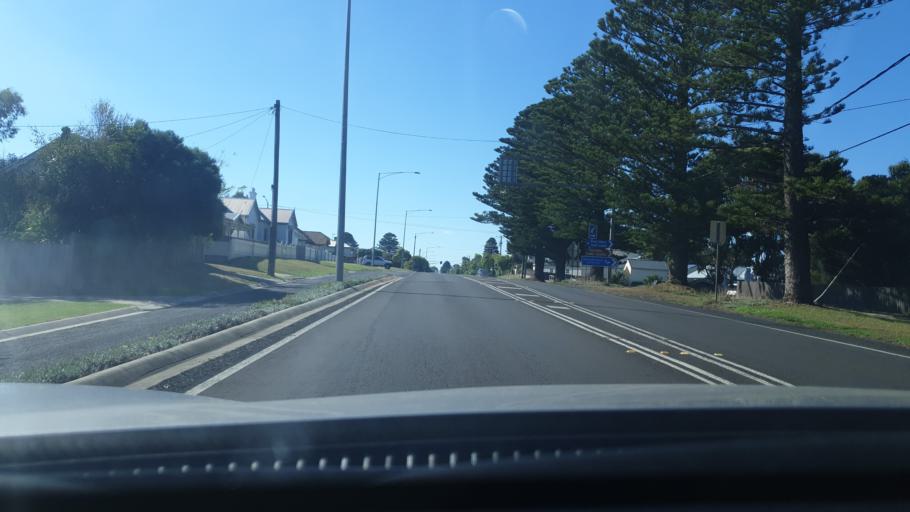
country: AU
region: Victoria
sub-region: Moyne
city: Port Fairy
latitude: -38.3837
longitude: 142.2289
